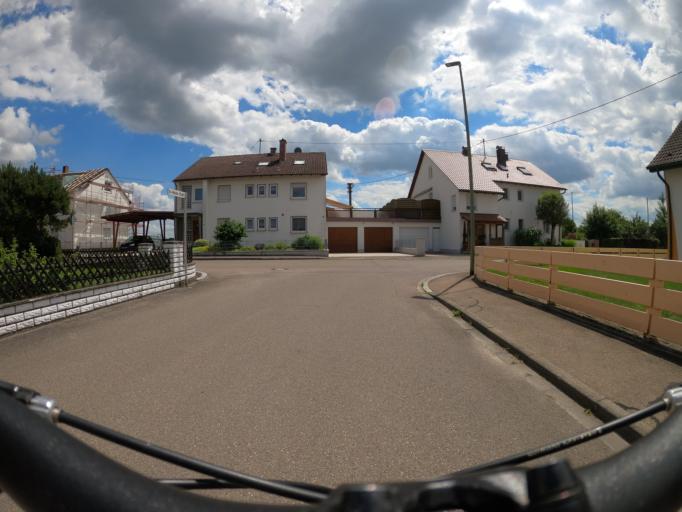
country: DE
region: Bavaria
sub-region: Swabia
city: Pfaffenhofen an der Roth
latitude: 48.3769
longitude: 10.1524
